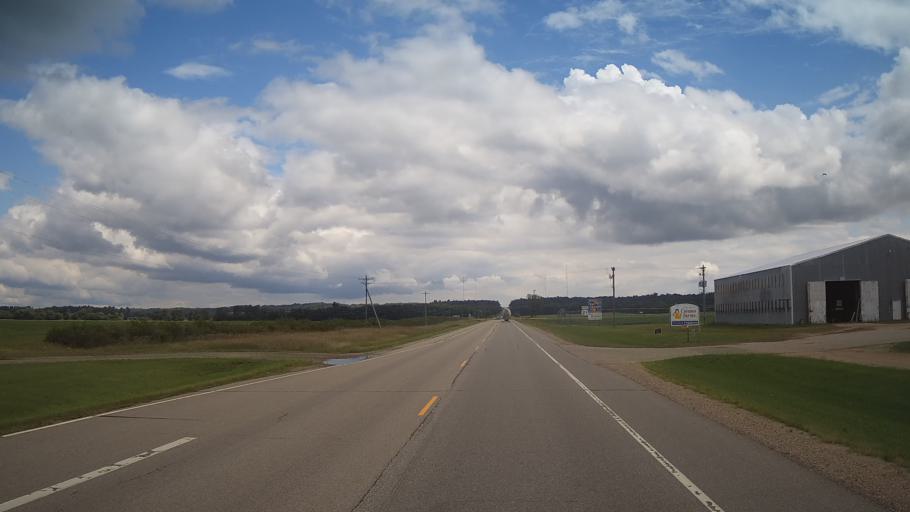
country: US
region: Wisconsin
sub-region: Marquette County
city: Westfield
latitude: 44.0221
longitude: -89.5968
